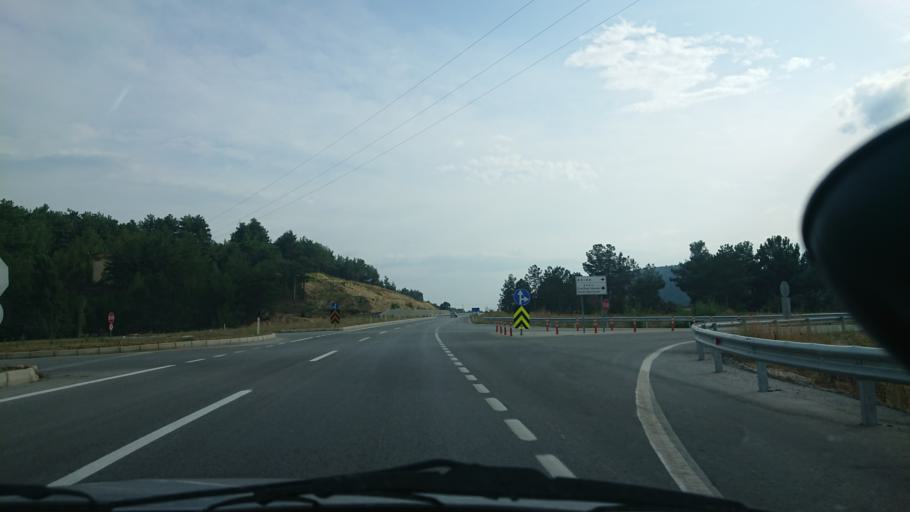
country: TR
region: Kuetahya
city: Gediz
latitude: 38.9259
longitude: 29.3047
